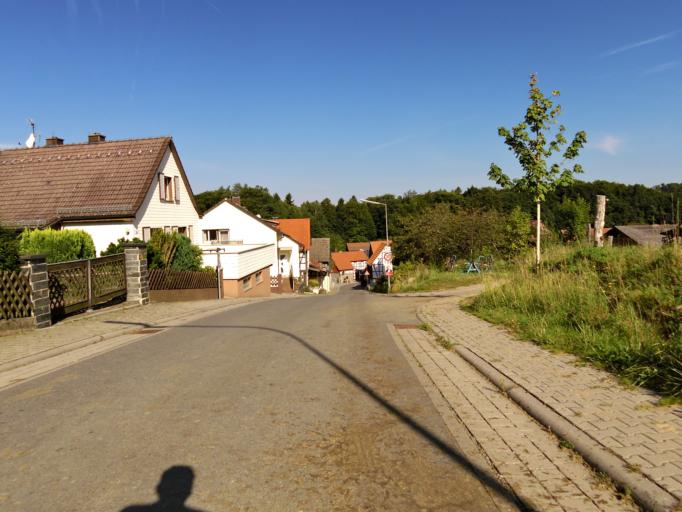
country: DE
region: Hesse
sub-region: Regierungsbezirk Darmstadt
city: Lindenfels
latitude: 49.6887
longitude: 8.7220
